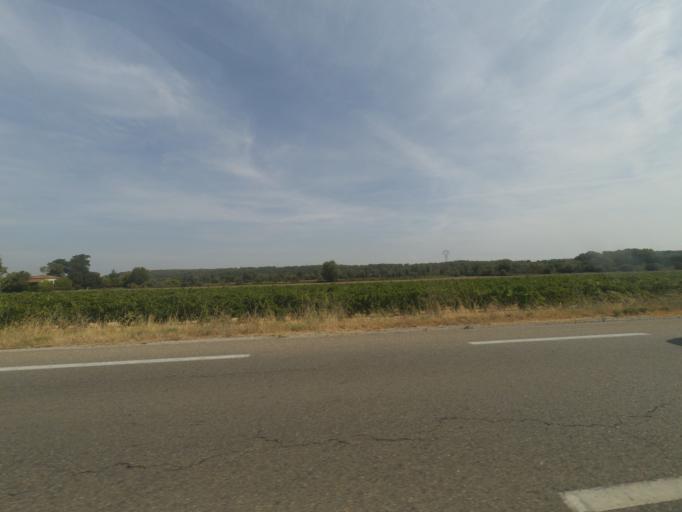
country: FR
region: Languedoc-Roussillon
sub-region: Departement du Gard
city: Mus
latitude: 43.7582
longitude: 4.2042
